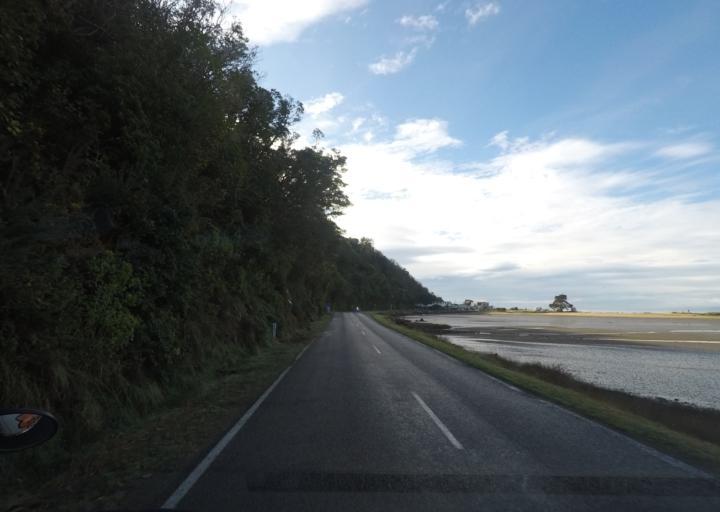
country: NZ
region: Tasman
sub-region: Tasman District
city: Motueka
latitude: -41.0100
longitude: 173.0045
